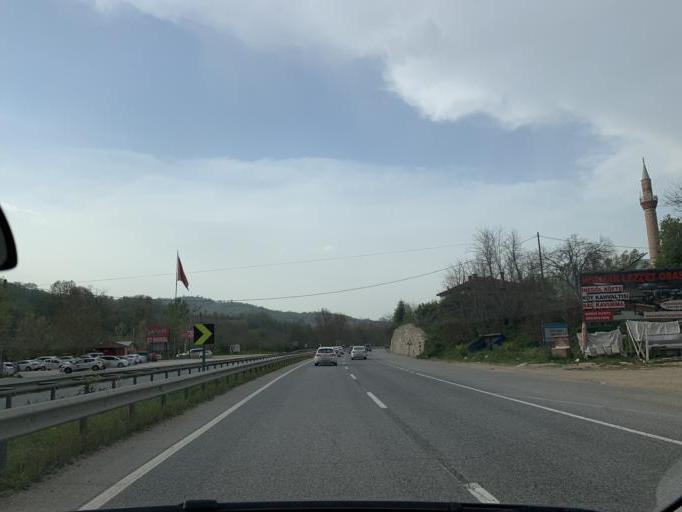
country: TR
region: Bursa
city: Tahtakopru
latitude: 39.9634
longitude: 29.6563
